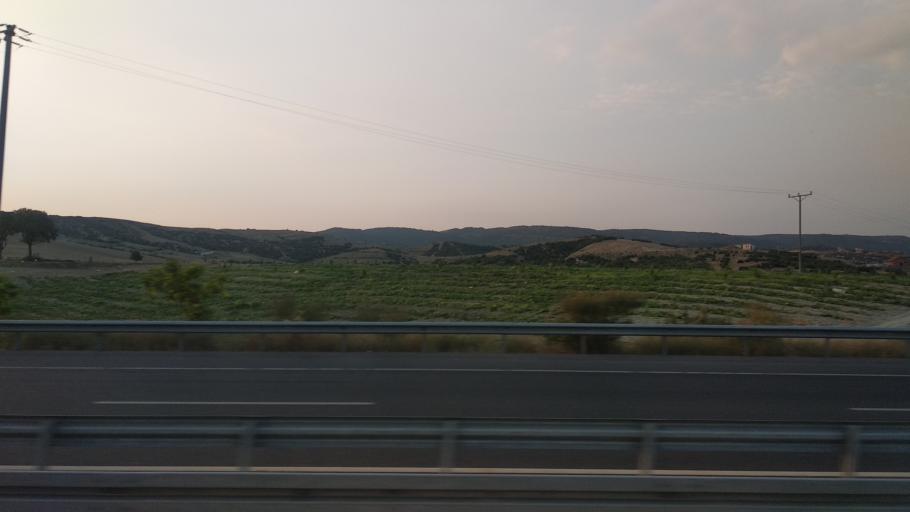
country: TR
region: Manisa
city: Selendi
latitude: 38.6234
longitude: 28.9272
